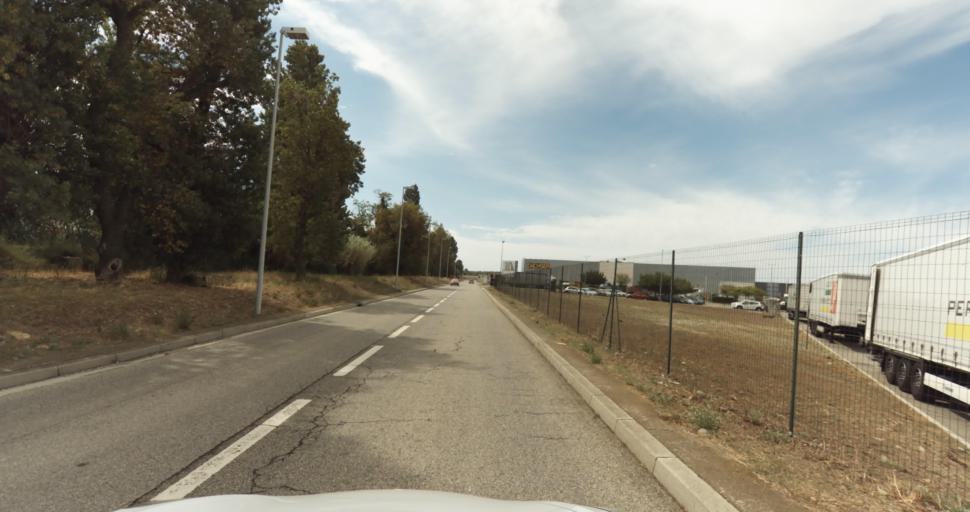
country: FR
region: Provence-Alpes-Cote d'Azur
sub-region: Departement des Bouches-du-Rhone
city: Miramas
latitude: 43.6047
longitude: 4.9996
